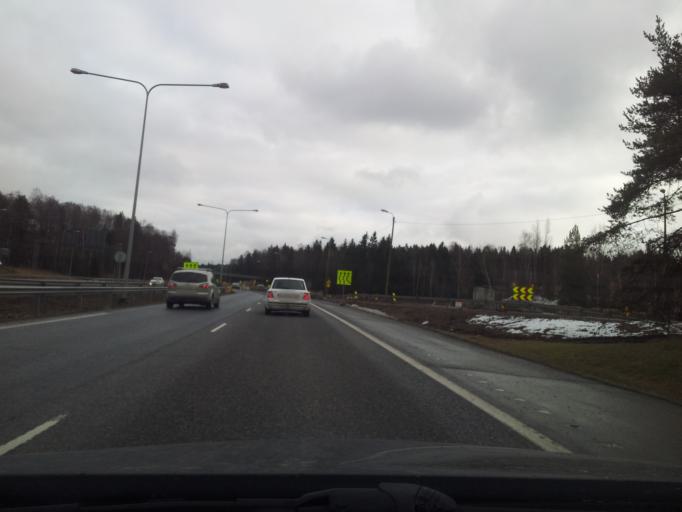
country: FI
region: Uusimaa
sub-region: Helsinki
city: Espoo
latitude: 60.1535
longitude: 24.6677
